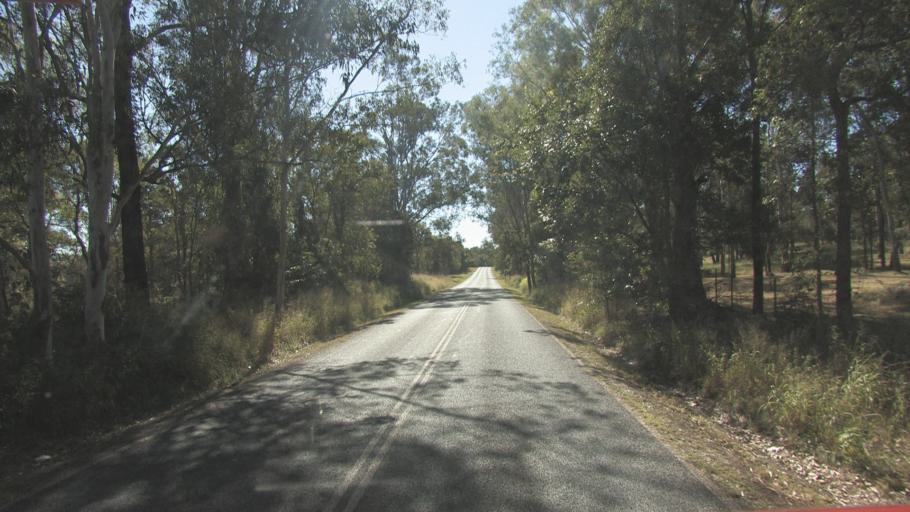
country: AU
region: Queensland
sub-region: Logan
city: Waterford West
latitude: -27.7146
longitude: 153.1415
